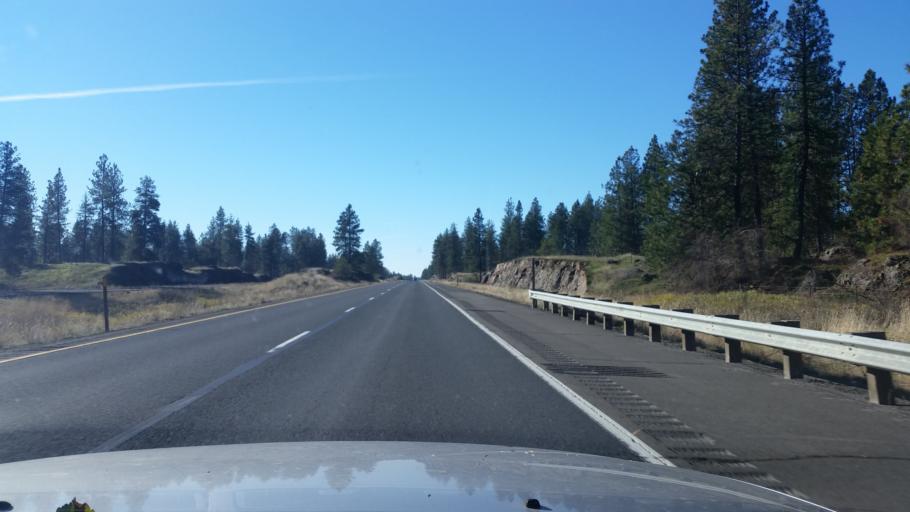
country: US
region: Washington
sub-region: Spokane County
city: Medical Lake
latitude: 47.5253
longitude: -117.6627
